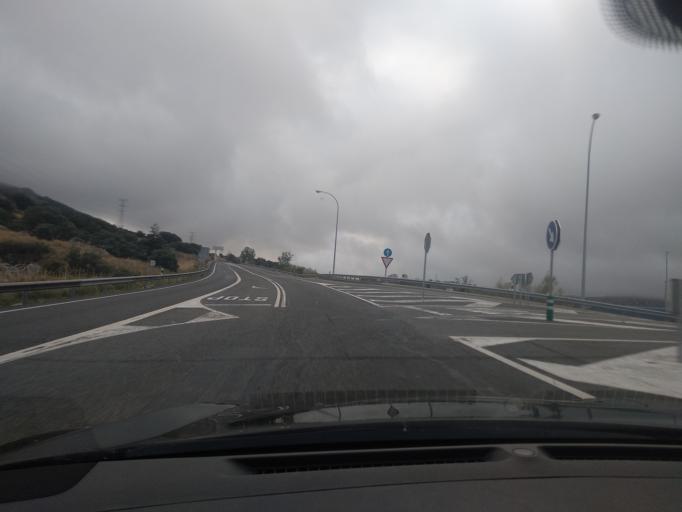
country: ES
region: Castille and Leon
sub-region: Provincia de Segovia
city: Otero de Herreros
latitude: 40.7908
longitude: -4.2151
